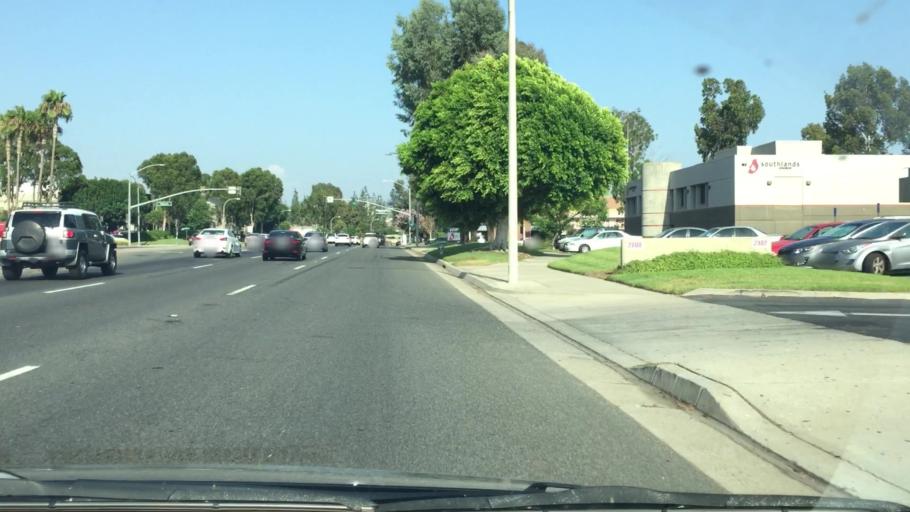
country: US
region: California
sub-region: Orange County
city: Placentia
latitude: 33.9109
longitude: -117.8587
